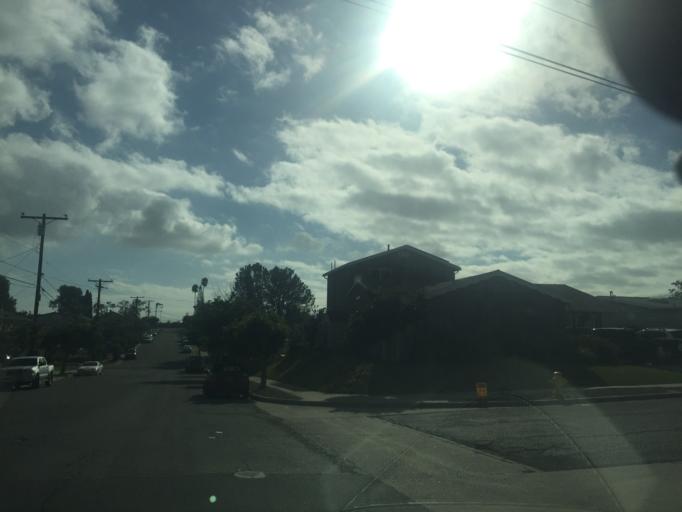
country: US
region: California
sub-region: San Diego County
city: San Diego
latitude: 32.7829
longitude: -117.1507
